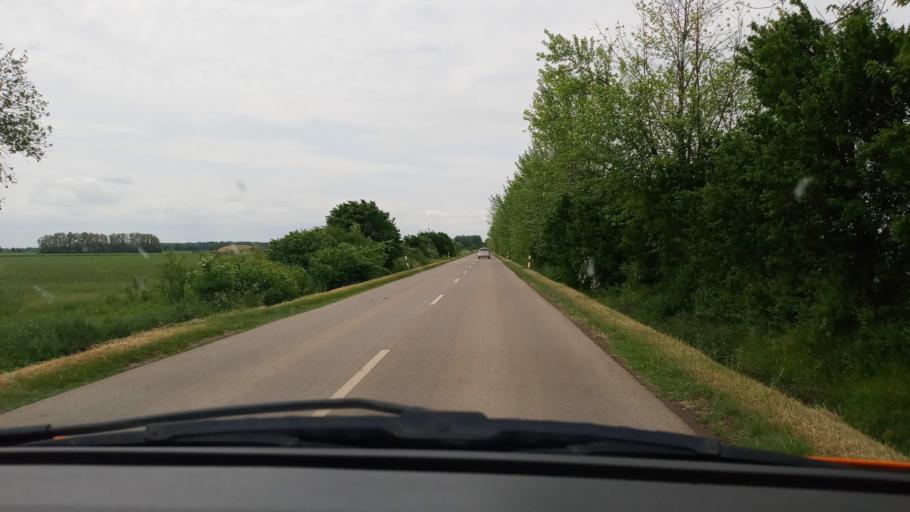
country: HU
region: Baranya
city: Vajszlo
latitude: 45.9165
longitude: 18.0545
